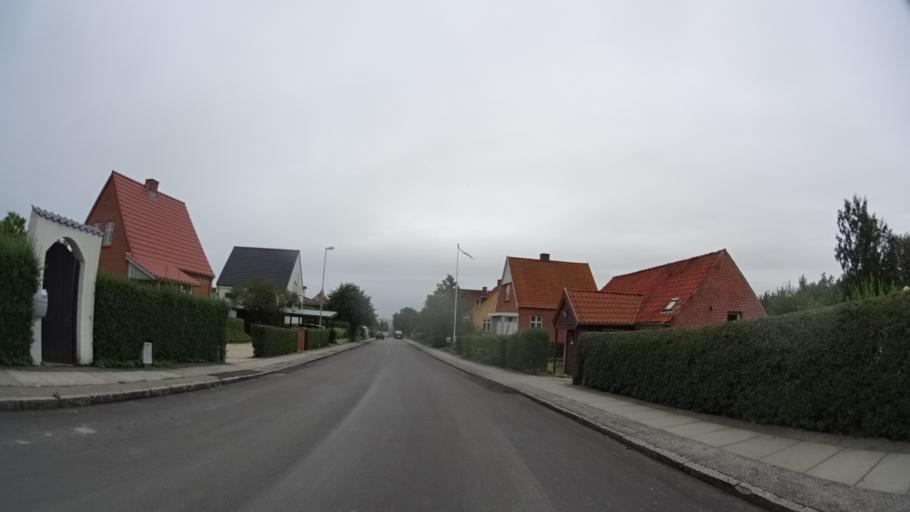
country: DK
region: Central Jutland
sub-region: Arhus Kommune
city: Stavtrup
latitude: 56.1583
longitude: 10.1445
